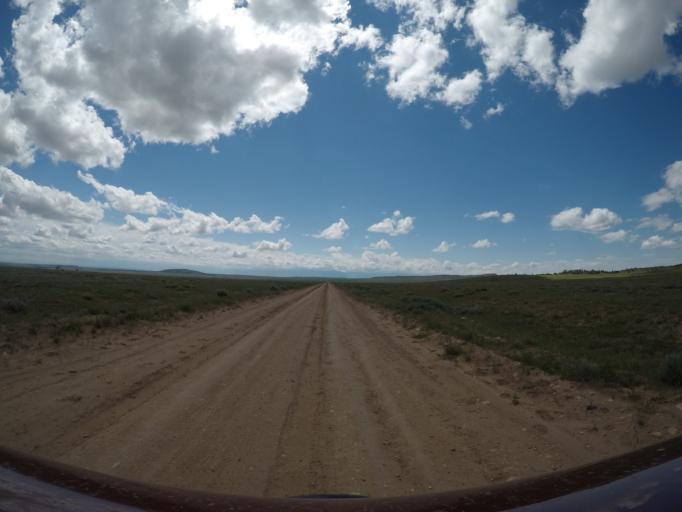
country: US
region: Montana
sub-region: Yellowstone County
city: Laurel
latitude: 45.2369
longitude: -108.6794
